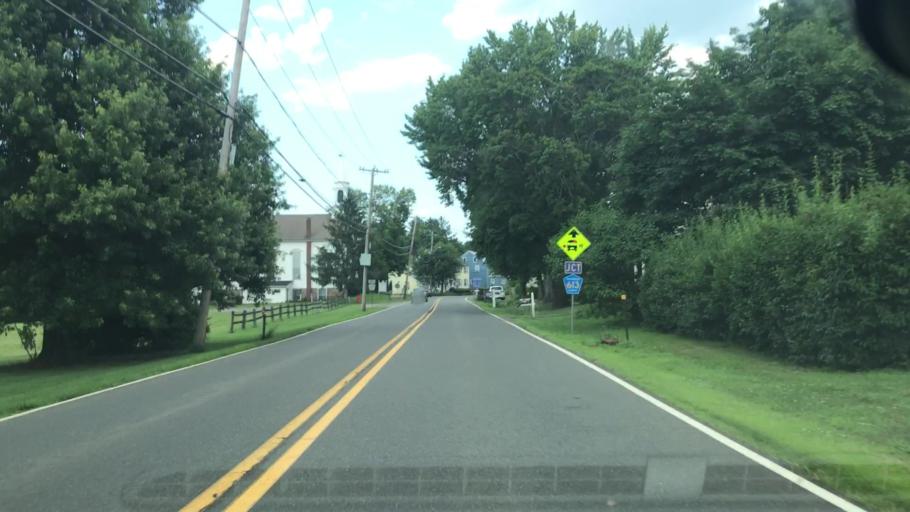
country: US
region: New Jersey
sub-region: Hunterdon County
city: Flemington
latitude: 40.4766
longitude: -74.8189
